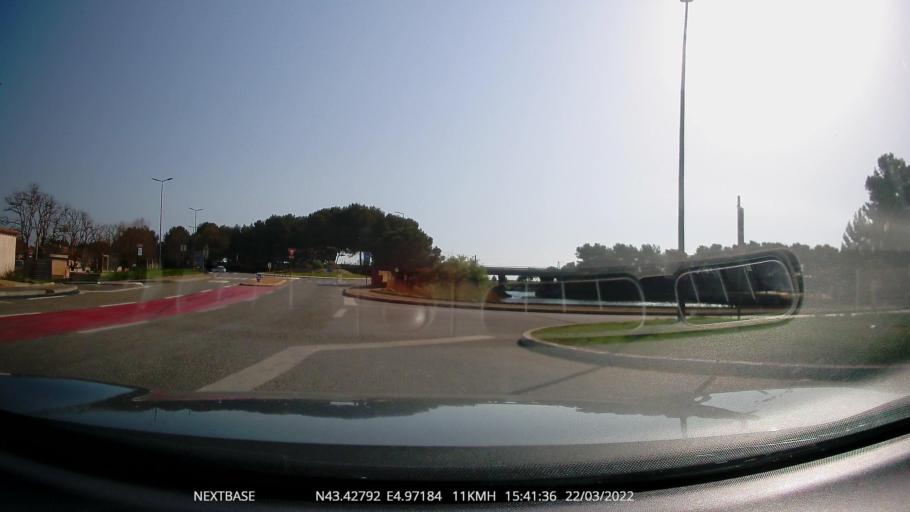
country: FR
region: Provence-Alpes-Cote d'Azur
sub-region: Departement des Bouches-du-Rhone
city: Port-de-Bouc
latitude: 43.4279
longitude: 4.9718
